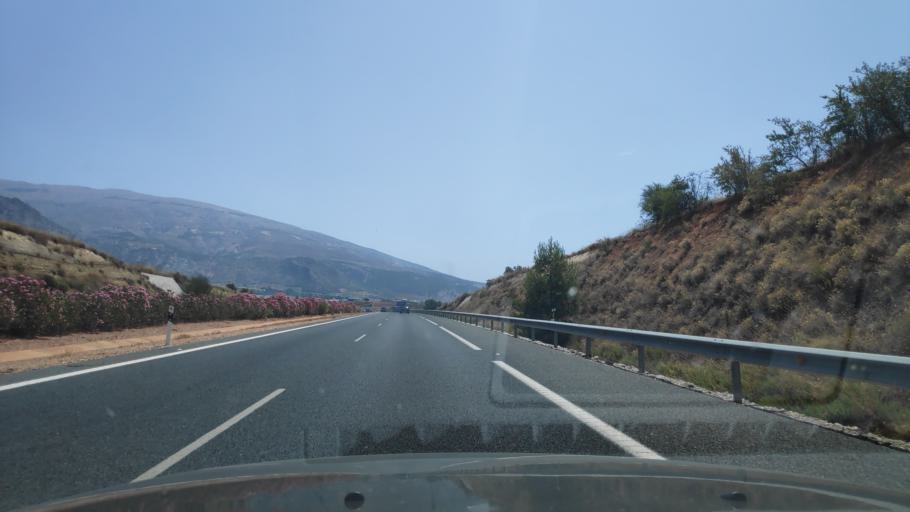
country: ES
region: Andalusia
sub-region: Provincia de Granada
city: Durcal
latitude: 36.9825
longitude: -3.5794
